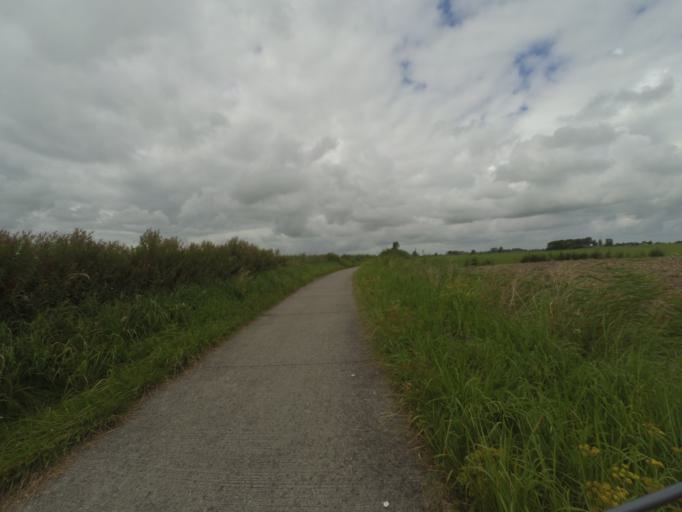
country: NL
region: Friesland
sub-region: Gemeente Kollumerland en Nieuwkruisland
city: Kollum
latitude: 53.3191
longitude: 6.1239
